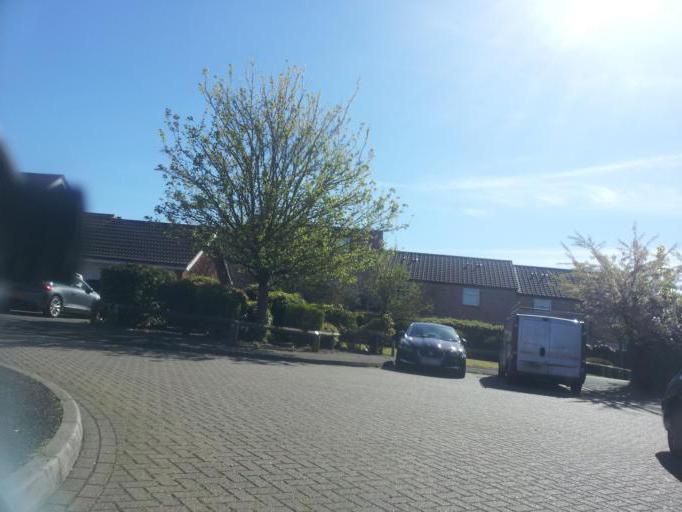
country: GB
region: England
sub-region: Kent
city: Rainham
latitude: 51.3681
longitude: 0.6228
